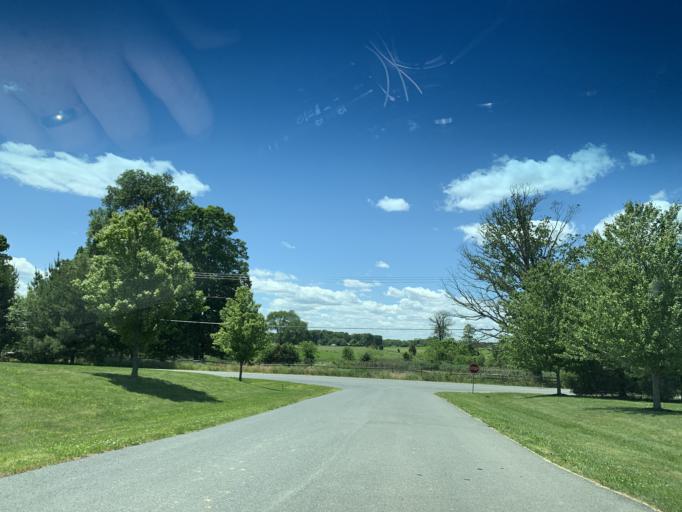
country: US
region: Maryland
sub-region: Cecil County
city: Rising Sun
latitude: 39.6763
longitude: -76.0169
